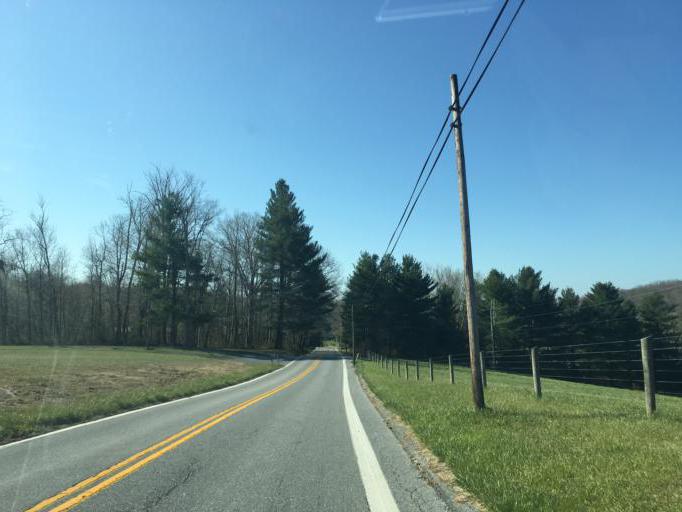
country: US
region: Maryland
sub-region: Washington County
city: Cavetown
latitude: 39.5946
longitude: -77.5587
